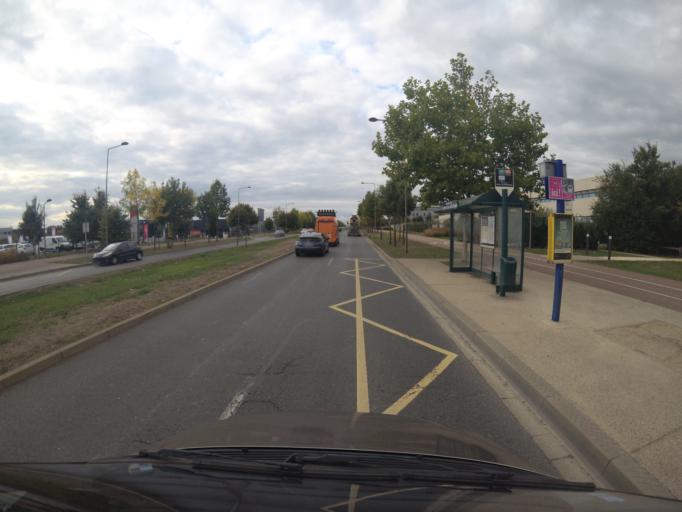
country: FR
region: Ile-de-France
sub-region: Departement de Seine-et-Marne
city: Chanteloup-en-Brie
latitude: 48.8526
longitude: 2.7621
